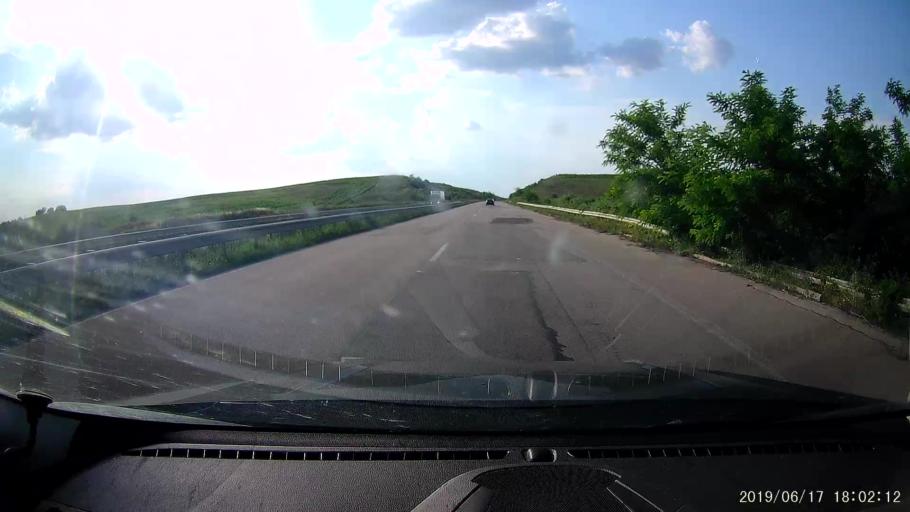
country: BG
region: Khaskovo
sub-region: Obshtina Svilengrad
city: Svilengrad
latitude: 41.7557
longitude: 26.2352
